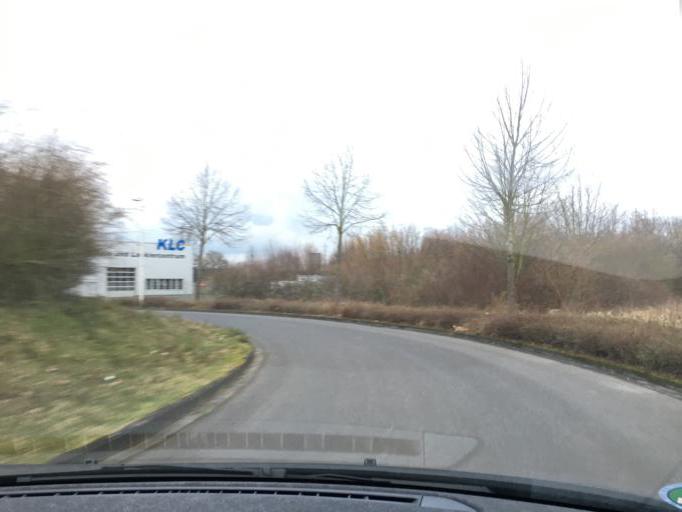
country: DE
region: North Rhine-Westphalia
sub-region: Regierungsbezirk Koln
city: Kerpen
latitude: 50.8940
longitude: 6.6850
